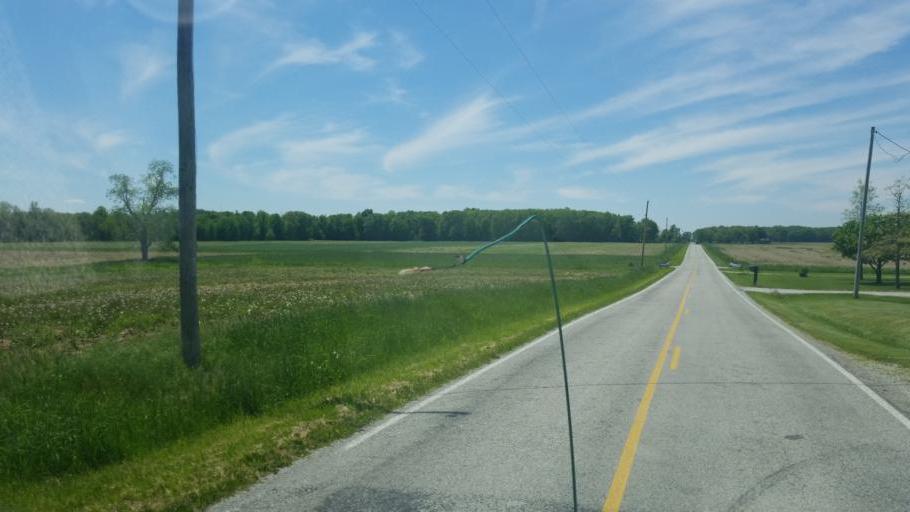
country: US
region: Ohio
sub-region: Huron County
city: Norwalk
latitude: 41.1892
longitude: -82.5408
